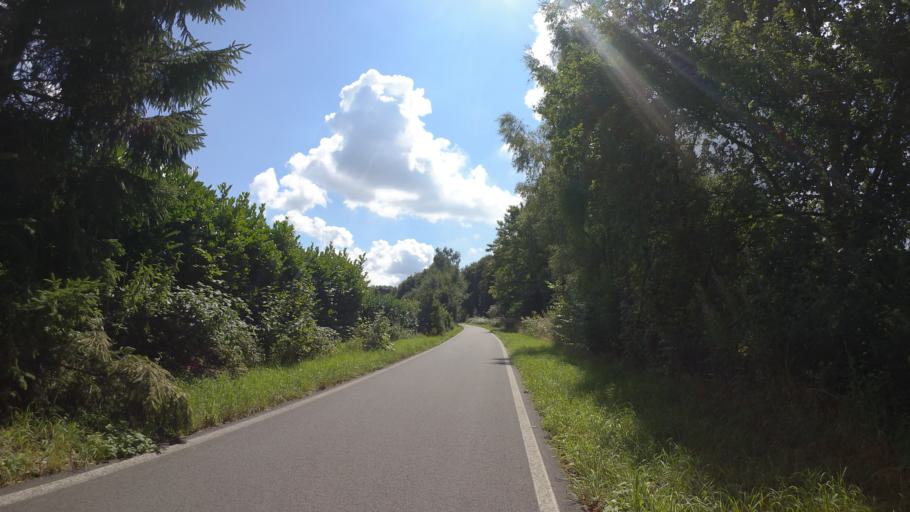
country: DE
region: North Rhine-Westphalia
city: Wermelskirchen
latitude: 51.1738
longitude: 7.2542
